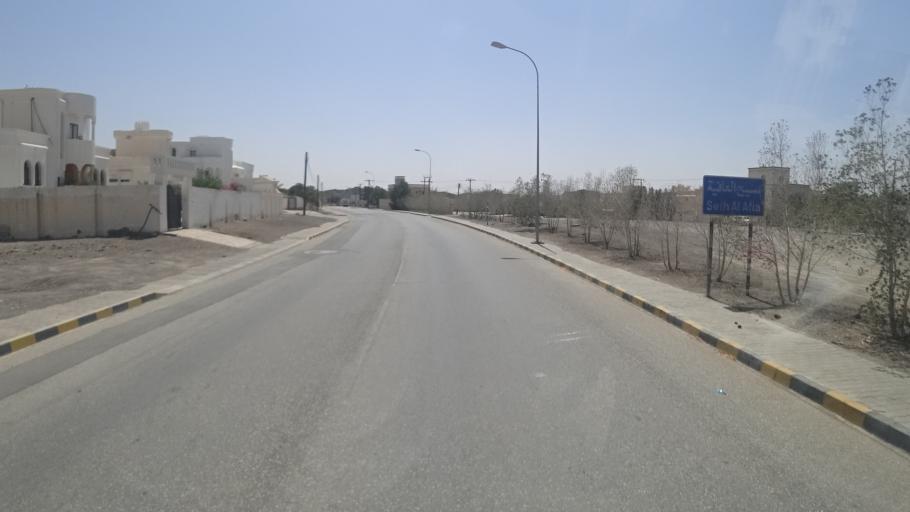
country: OM
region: Ash Sharqiyah
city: Ibra'
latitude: 22.6850
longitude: 58.5441
